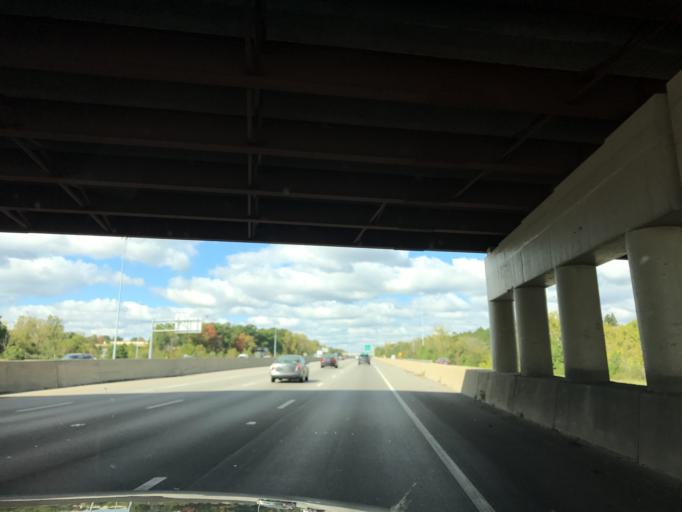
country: US
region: Ohio
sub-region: Franklin County
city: Westerville
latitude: 40.1055
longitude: -82.9491
